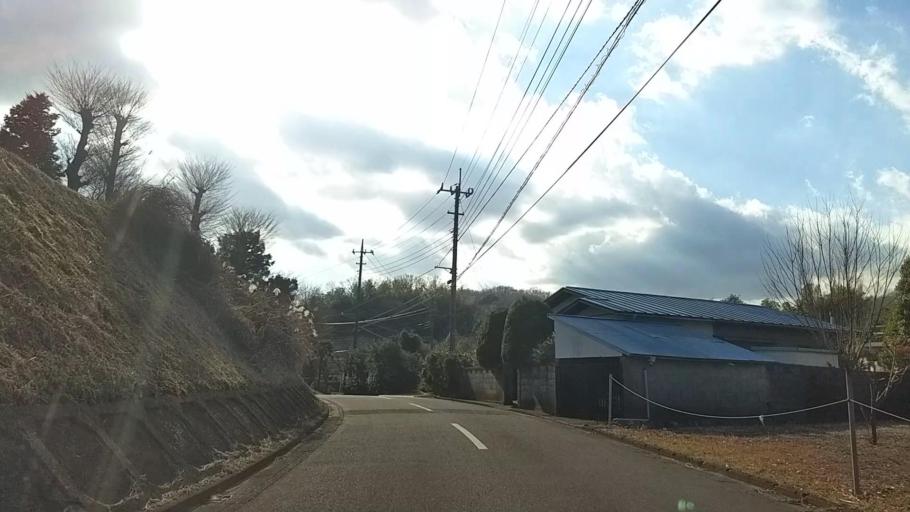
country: JP
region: Kanagawa
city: Isehara
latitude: 35.4301
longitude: 139.3175
